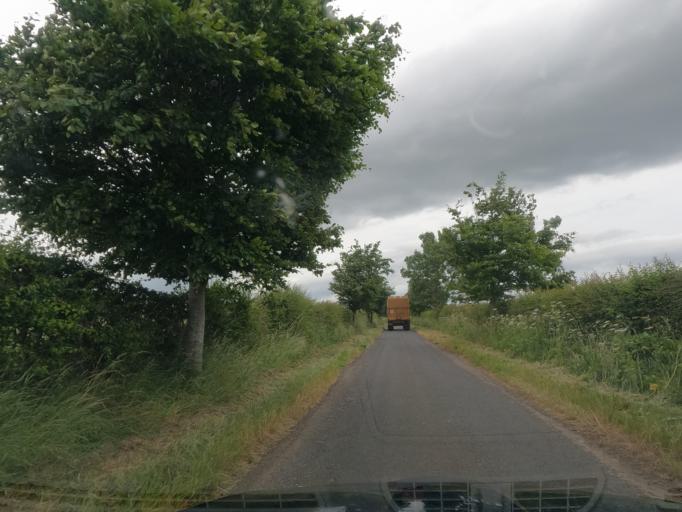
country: GB
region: England
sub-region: Northumberland
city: Lowick
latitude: 55.5765
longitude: -1.9203
